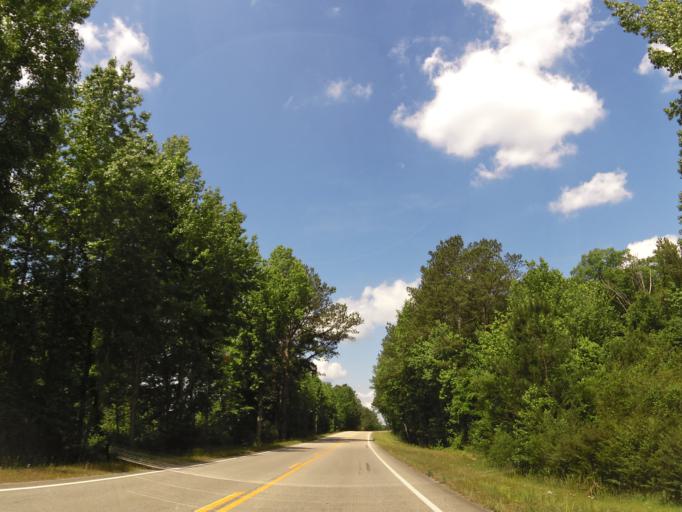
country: US
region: Alabama
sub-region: Marion County
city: Guin
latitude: 33.9552
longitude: -87.9286
